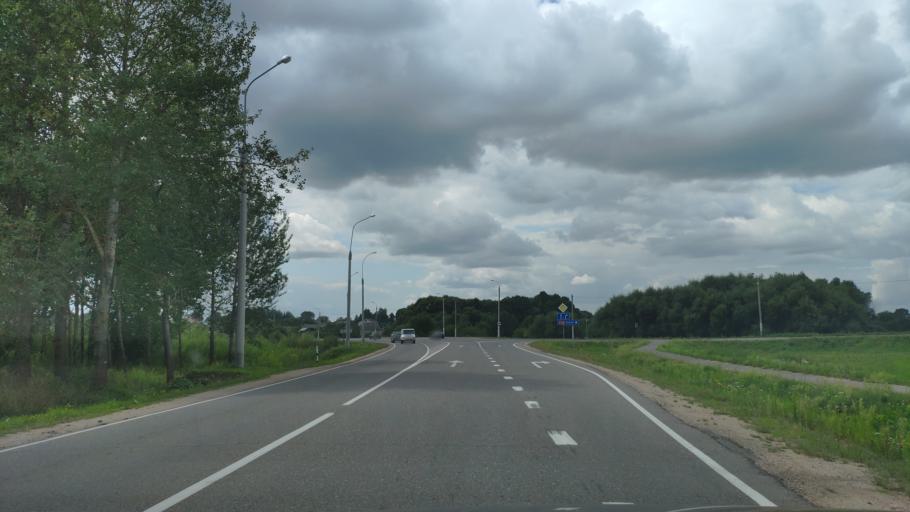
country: BY
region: Minsk
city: Zaslawye
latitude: 54.0066
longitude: 27.3050
